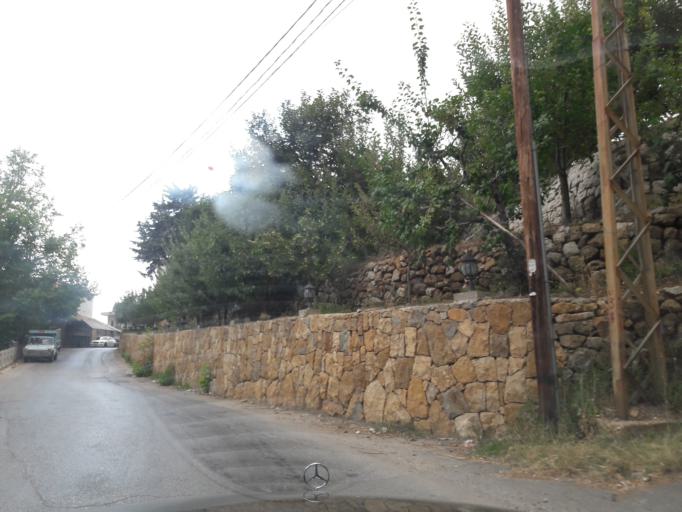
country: LB
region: Beqaa
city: Zahle
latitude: 33.9437
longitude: 35.7983
